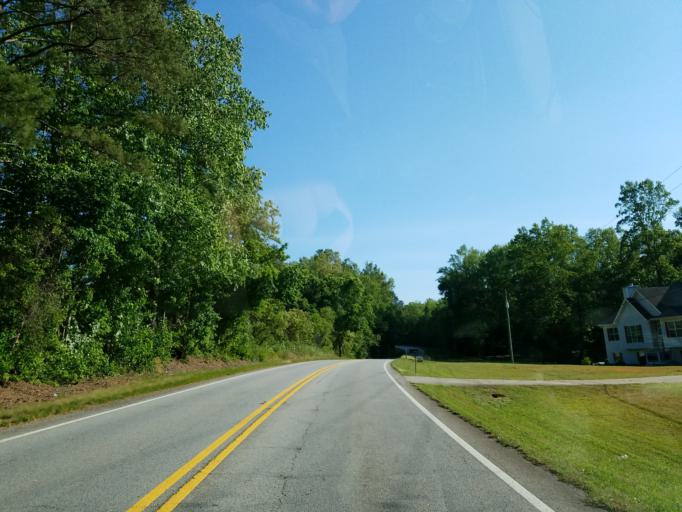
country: US
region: Georgia
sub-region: Carroll County
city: Temple
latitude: 33.8159
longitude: -84.9741
